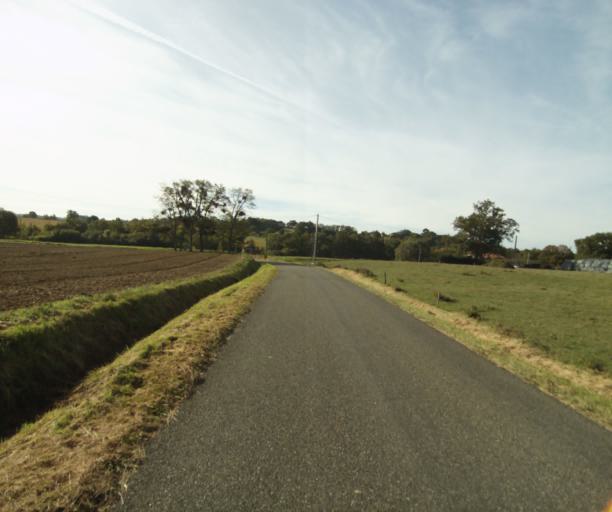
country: FR
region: Midi-Pyrenees
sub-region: Departement du Gers
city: Eauze
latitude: 43.9010
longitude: 0.1376
